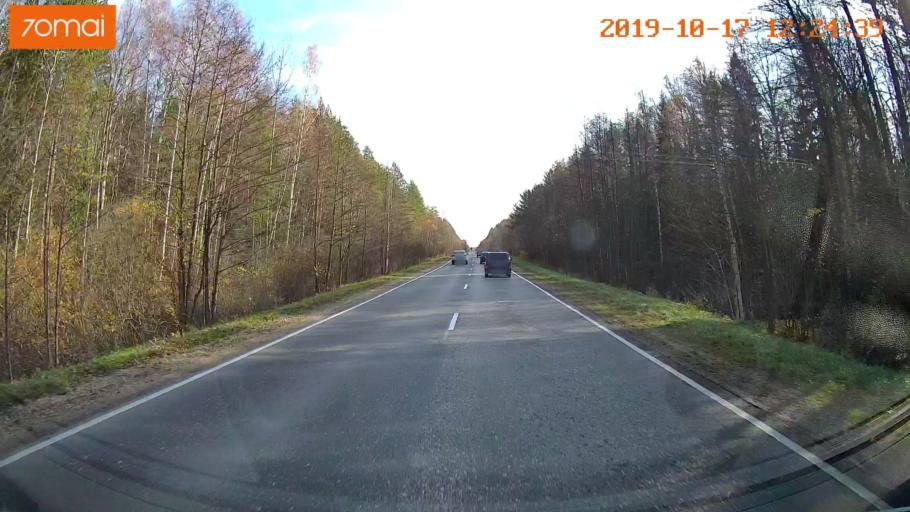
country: RU
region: Rjazan
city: Gus'-Zheleznyy
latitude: 55.0338
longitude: 41.2193
